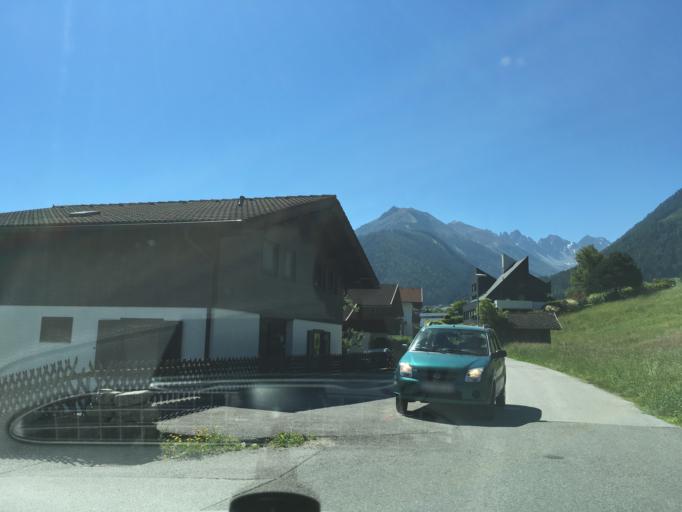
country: AT
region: Tyrol
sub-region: Politischer Bezirk Innsbruck Land
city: Oberperfuss
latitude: 47.2390
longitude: 11.2439
